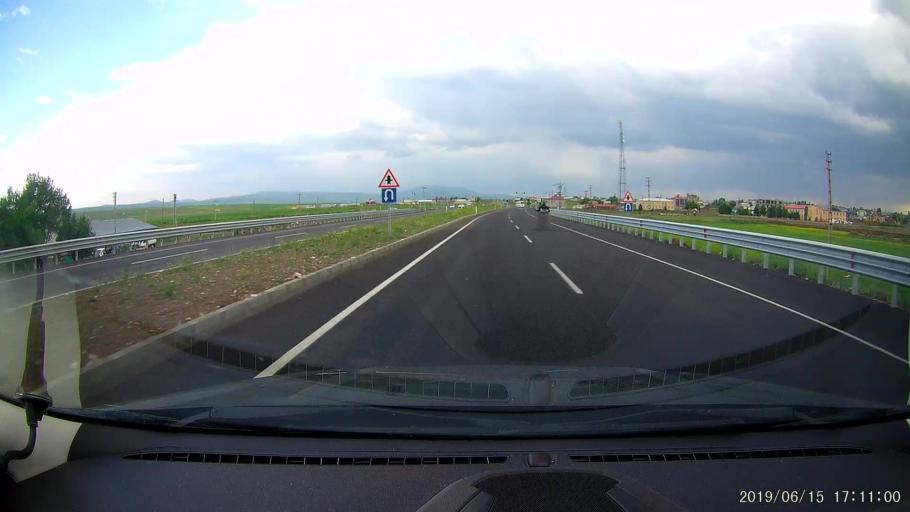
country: TR
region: Kars
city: Kars
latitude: 40.6160
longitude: 43.1334
